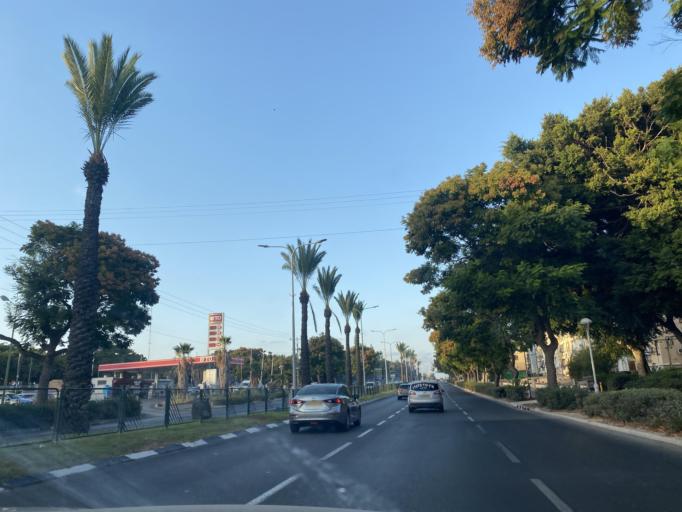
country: IL
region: Southern District
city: Ashdod
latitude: 31.7957
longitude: 34.6526
